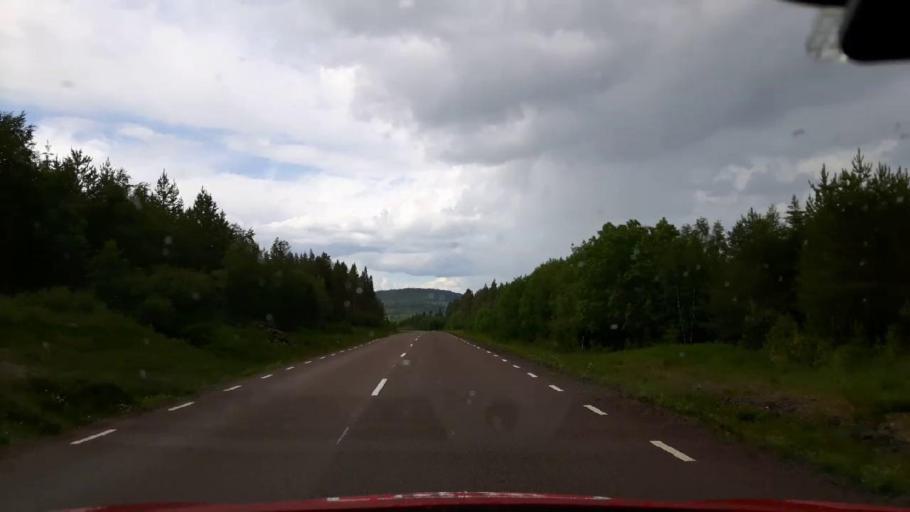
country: SE
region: Jaemtland
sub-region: Krokoms Kommun
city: Valla
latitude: 63.8928
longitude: 14.2632
